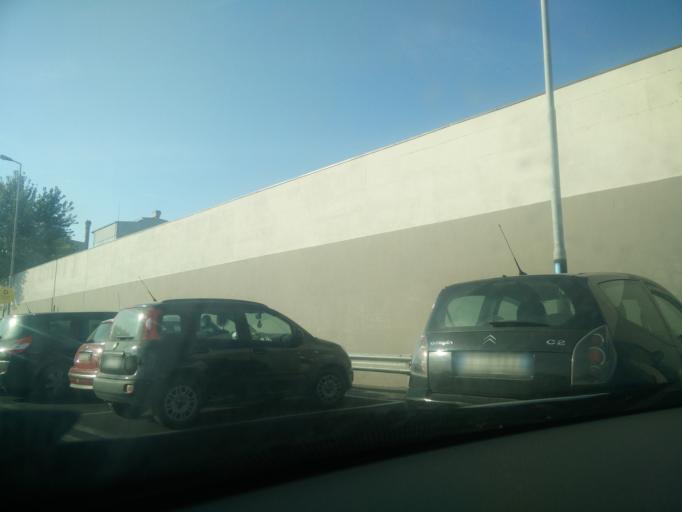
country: IT
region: Tuscany
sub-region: Provincia di Massa-Carrara
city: Massa
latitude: 44.0218
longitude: 10.1119
